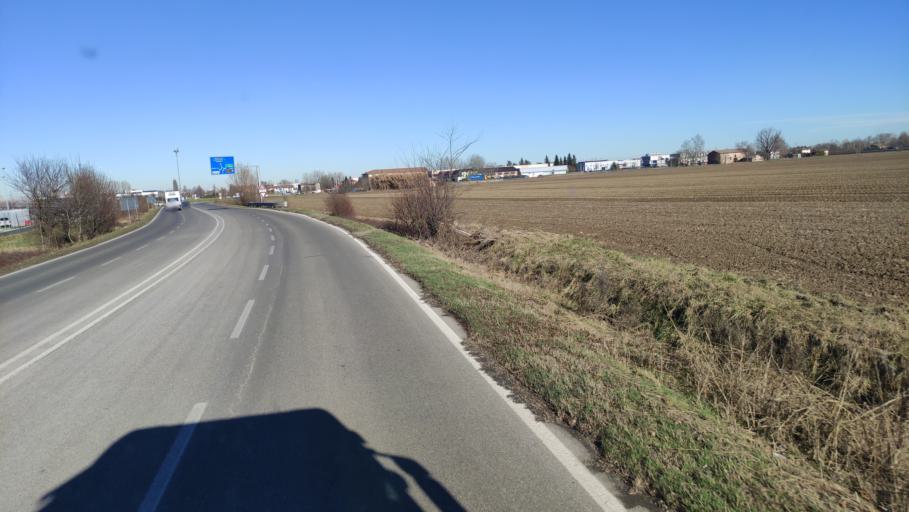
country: IT
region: Emilia-Romagna
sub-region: Provincia di Reggio Emilia
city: Correggio
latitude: 44.7637
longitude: 10.8110
